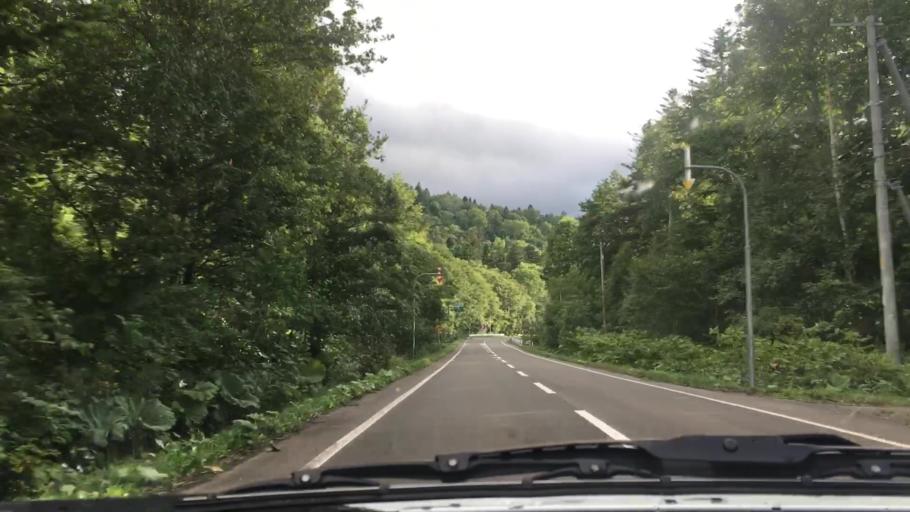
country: JP
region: Hokkaido
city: Shimo-furano
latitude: 43.0883
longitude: 142.6799
